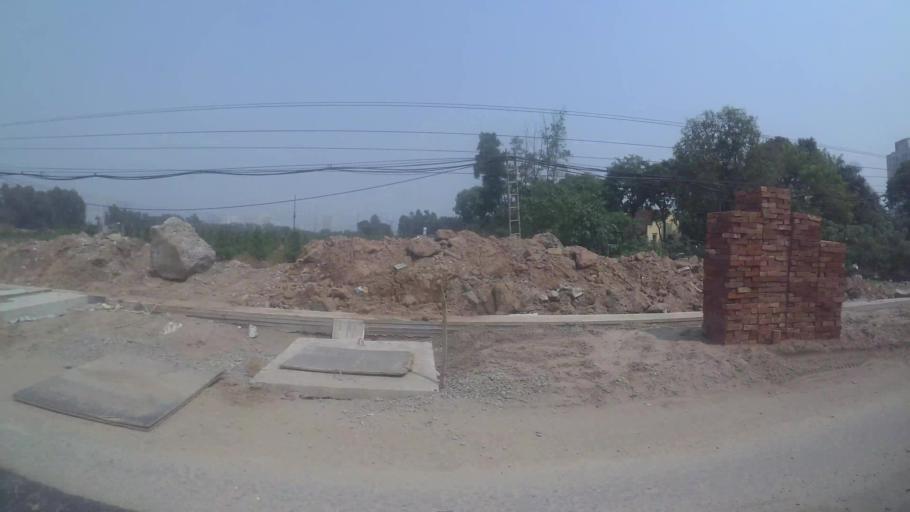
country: VN
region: Ha Noi
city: Ha Dong
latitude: 20.9954
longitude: 105.7620
